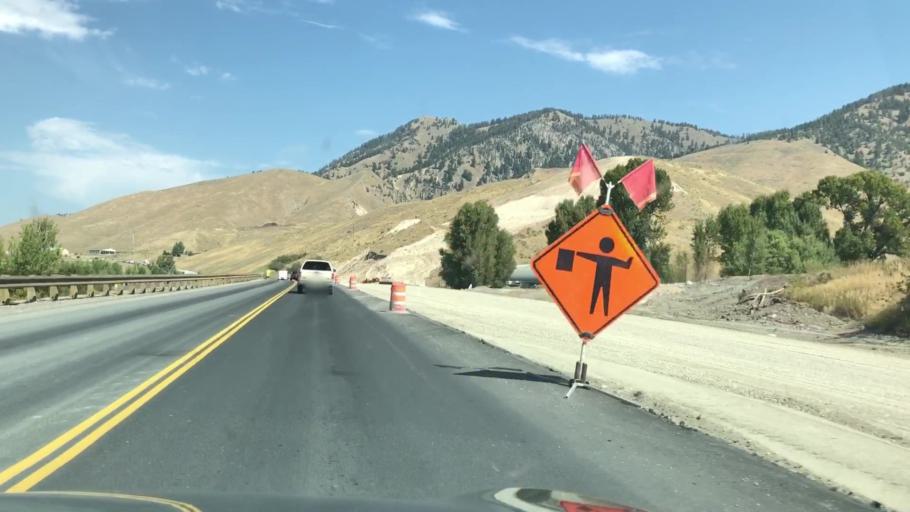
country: US
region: Wyoming
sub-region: Teton County
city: South Park
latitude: 43.3918
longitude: -110.7476
